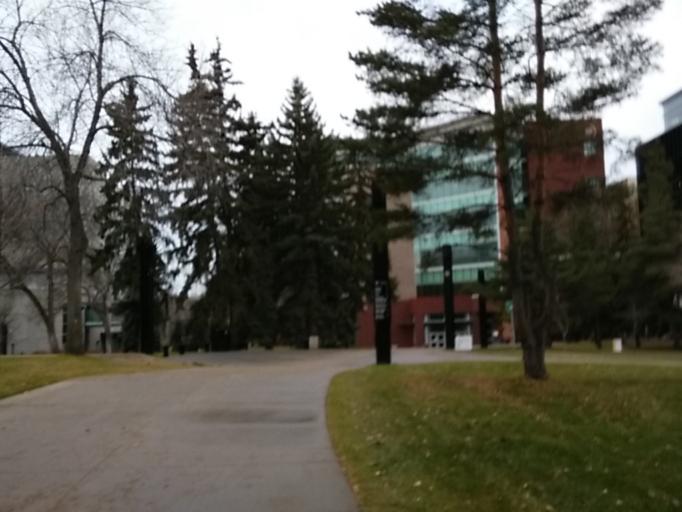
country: CA
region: Alberta
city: Edmonton
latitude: 53.5272
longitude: -113.5272
